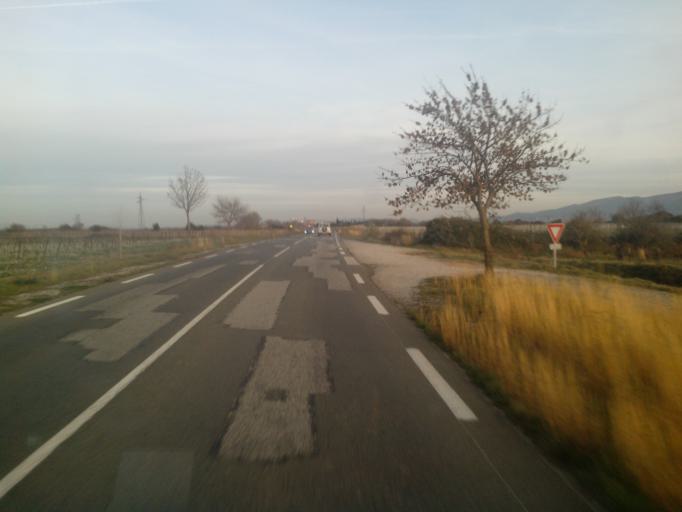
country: FR
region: Languedoc-Roussillon
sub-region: Departement de l'Aude
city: Capendu
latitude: 43.2034
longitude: 2.5217
